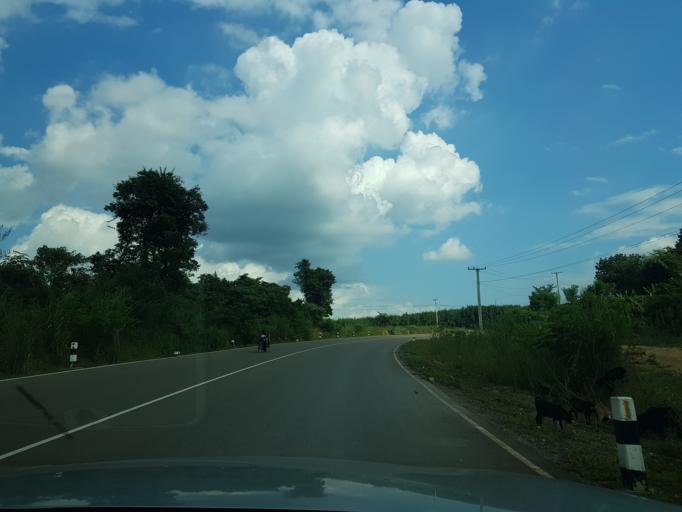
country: TH
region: Nong Khai
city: Sangkhom
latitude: 18.0374
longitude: 102.3631
